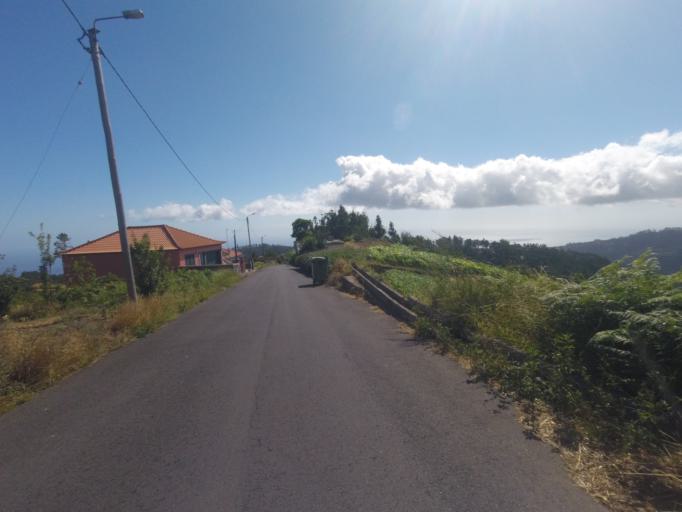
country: PT
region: Madeira
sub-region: Ribeira Brava
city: Campanario
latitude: 32.7004
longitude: -17.0228
